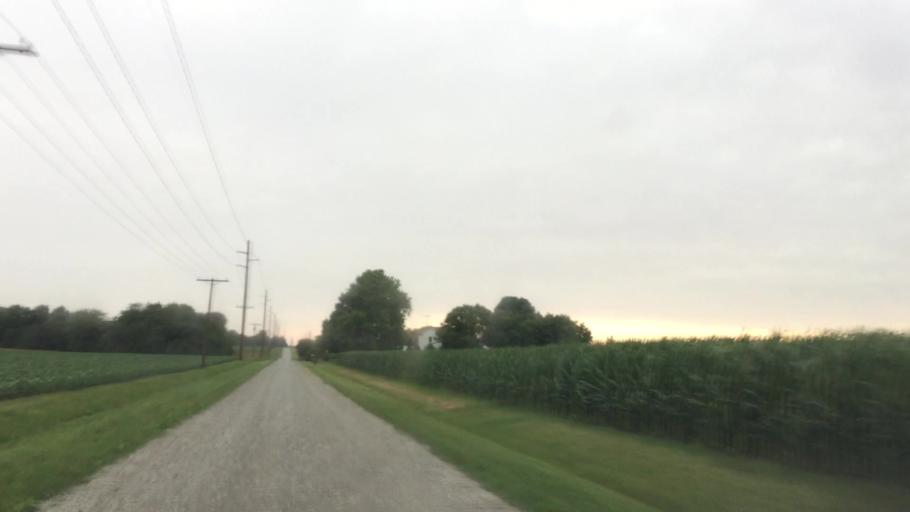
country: US
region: Iowa
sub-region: Lee County
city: Fort Madison
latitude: 40.5963
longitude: -91.2678
